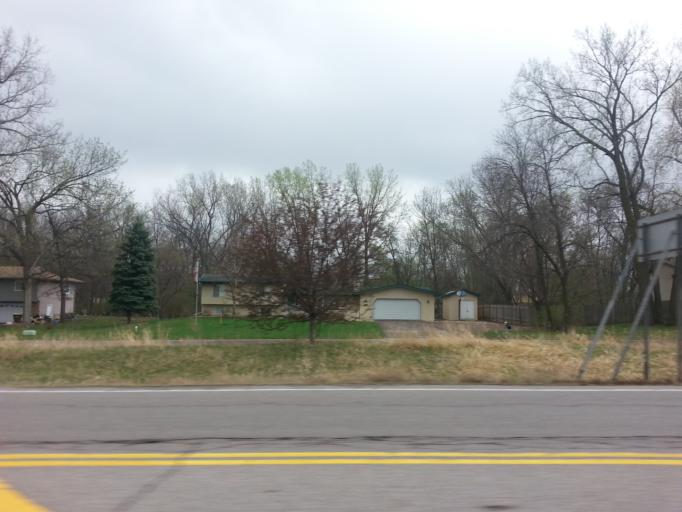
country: US
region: Minnesota
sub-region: Scott County
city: Prior Lake
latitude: 44.7310
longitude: -93.3917
